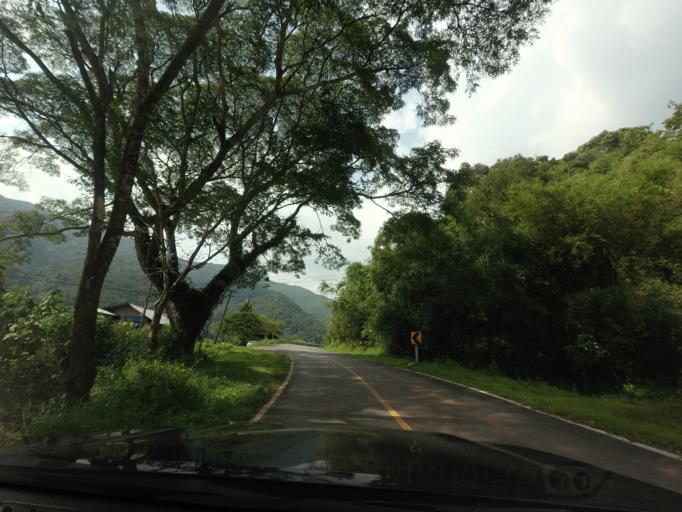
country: TH
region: Nan
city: Bo Kluea
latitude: 19.1544
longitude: 101.1582
